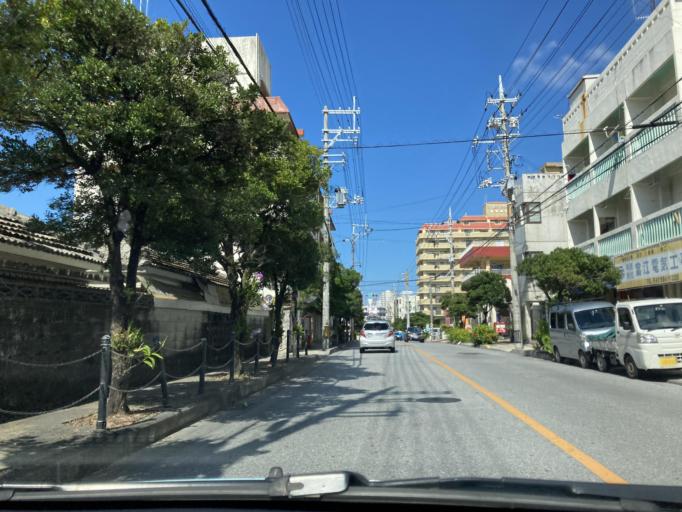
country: JP
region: Okinawa
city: Naha-shi
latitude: 26.2165
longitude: 127.7091
